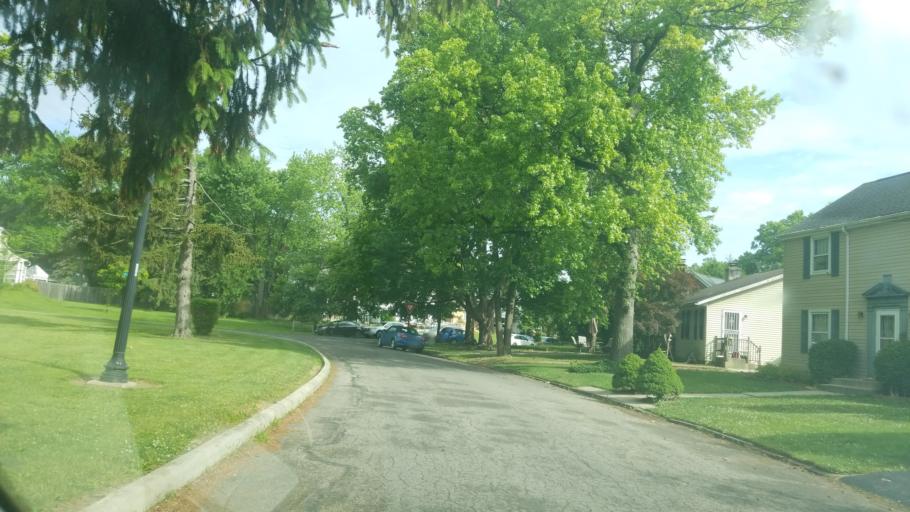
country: US
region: Ohio
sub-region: Franklin County
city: Minerva Park
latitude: 40.0241
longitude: -82.9708
